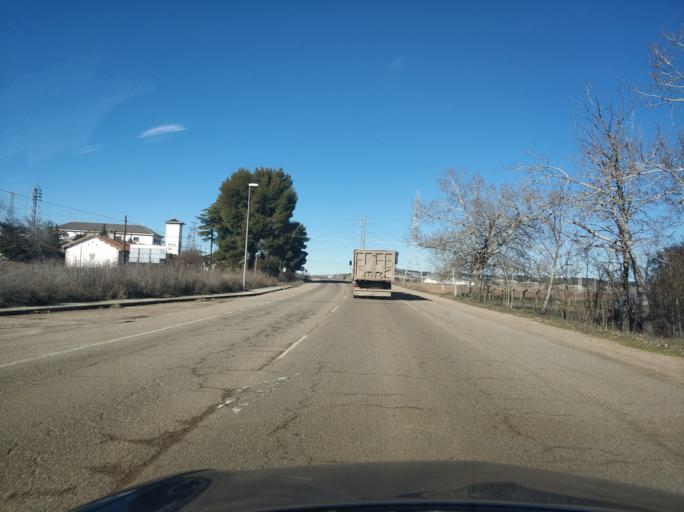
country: ES
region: Castille and Leon
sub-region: Provincia de Valladolid
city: Tordesillas
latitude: 41.5062
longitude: -5.0093
